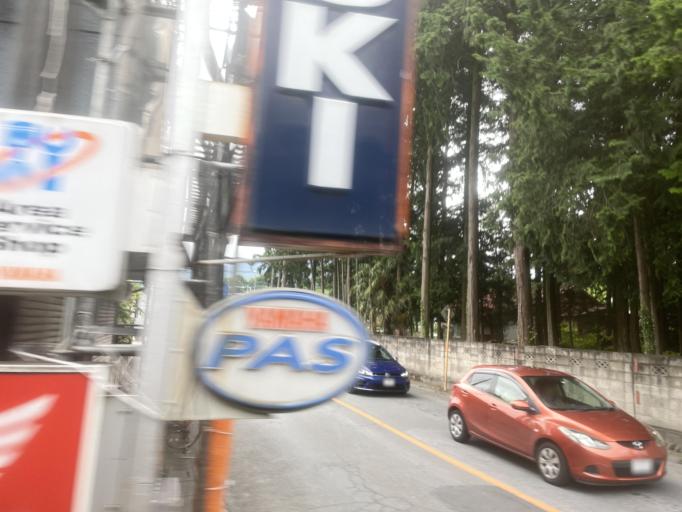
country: JP
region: Saitama
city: Chichibu
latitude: 36.0205
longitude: 139.0957
